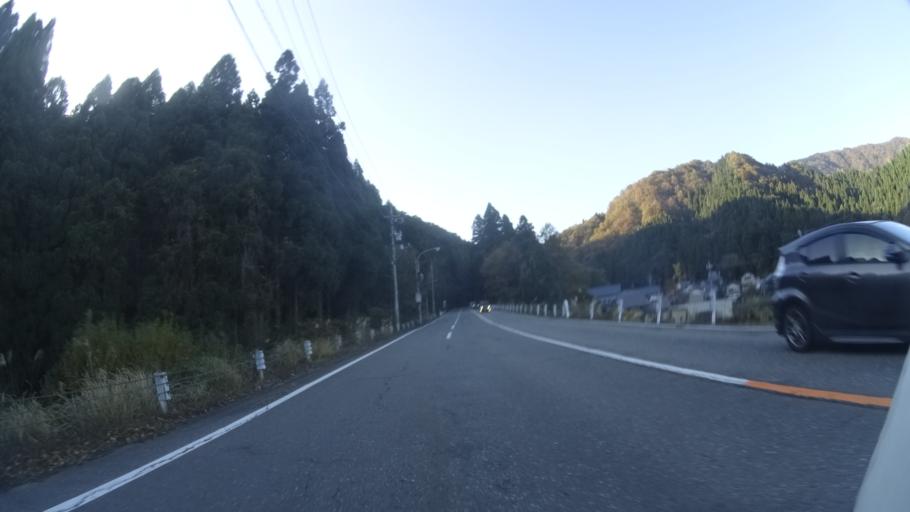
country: JP
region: Fukui
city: Ono
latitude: 35.9961
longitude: 136.4579
